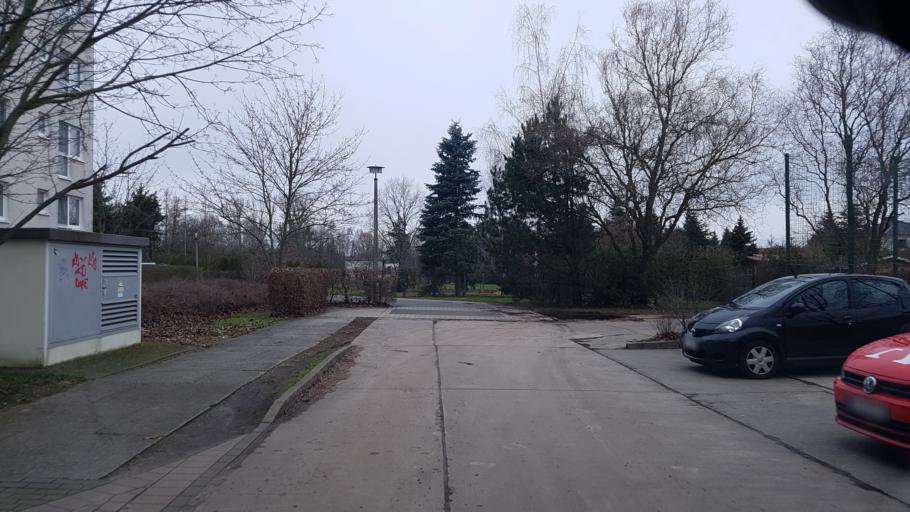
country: DE
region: Brandenburg
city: Herzberg
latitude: 51.6965
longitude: 13.2341
